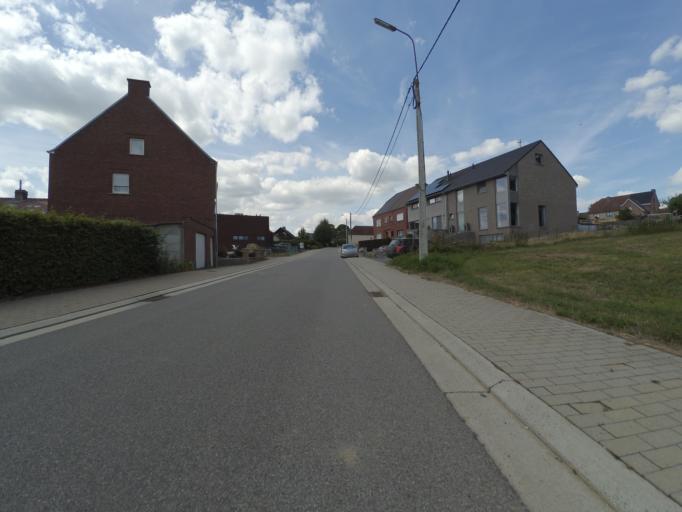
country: BE
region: Flanders
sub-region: Provincie Oost-Vlaanderen
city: Zottegem
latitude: 50.8491
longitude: 3.7576
